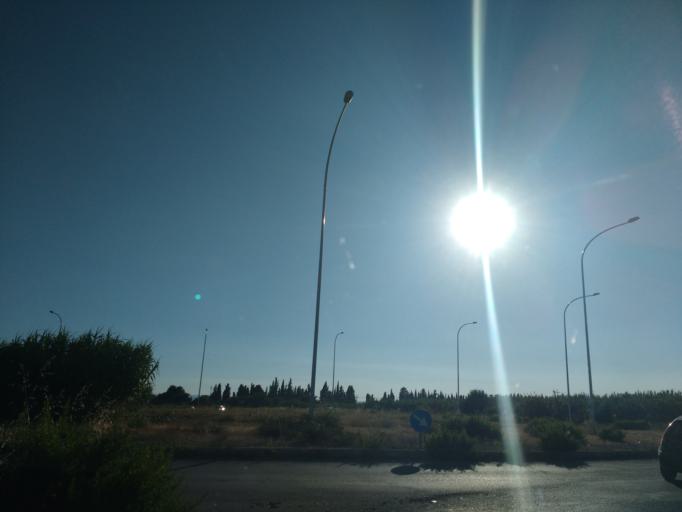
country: IT
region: Sicily
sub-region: Provincia di Siracusa
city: Siracusa
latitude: 37.0649
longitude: 15.2464
